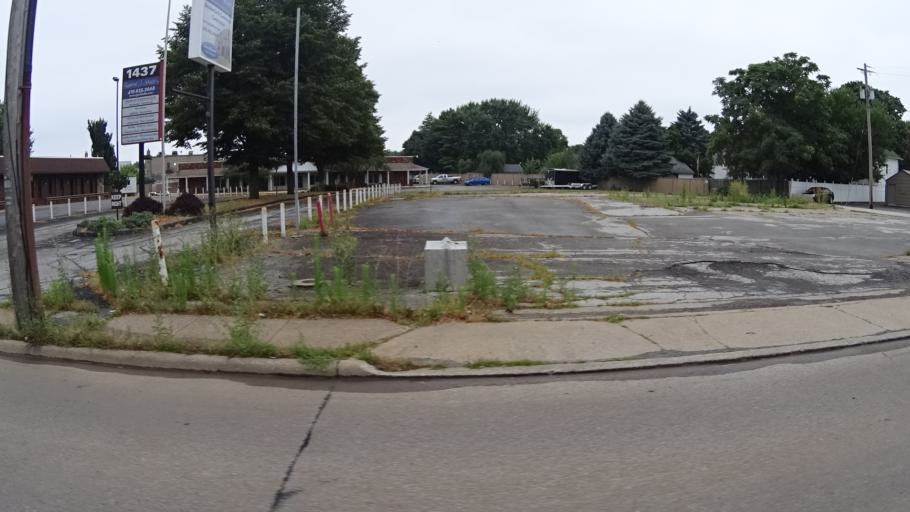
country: US
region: Ohio
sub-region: Erie County
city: Sandusky
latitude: 41.4454
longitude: -82.6975
